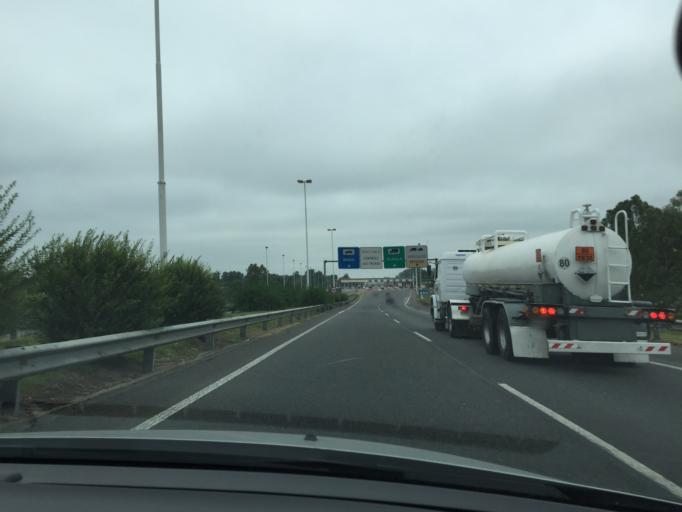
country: AR
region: Buenos Aires
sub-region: Partido de Ezeiza
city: Ezeiza
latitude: -34.8516
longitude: -58.5470
